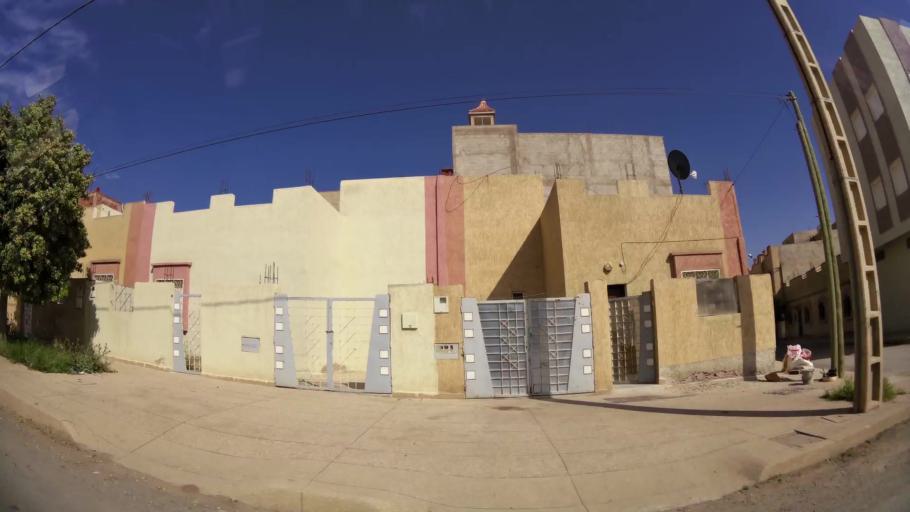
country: MA
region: Oriental
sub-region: Oujda-Angad
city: Oujda
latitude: 34.7100
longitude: -1.8846
